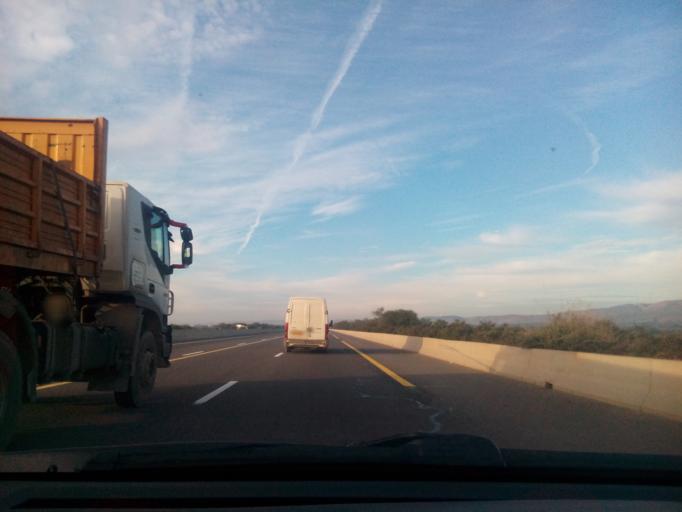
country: DZ
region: Relizane
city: Relizane
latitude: 35.7914
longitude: 0.4304
